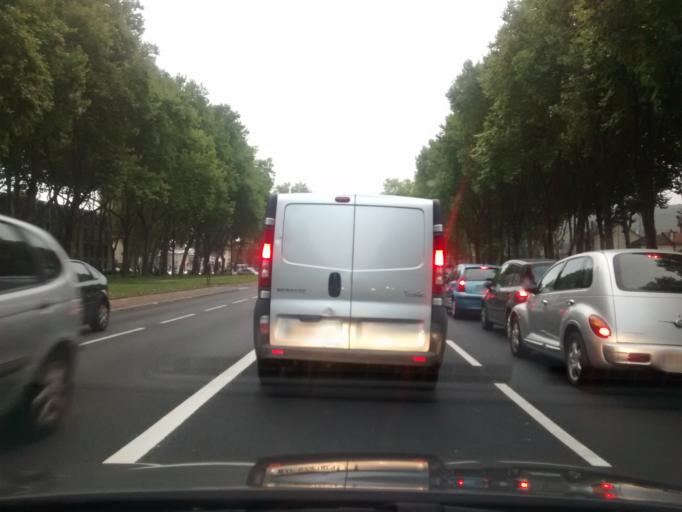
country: FR
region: Ile-de-France
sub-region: Departement des Yvelines
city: Viroflay
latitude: 48.7984
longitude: 2.1563
